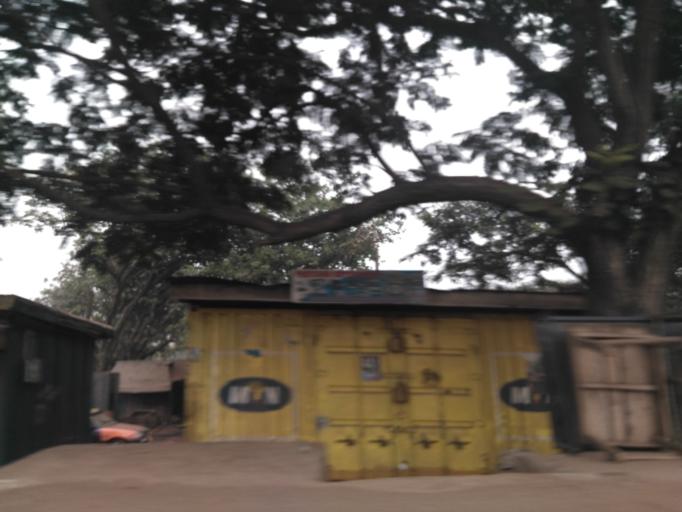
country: GH
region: Ashanti
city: Kumasi
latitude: 6.7101
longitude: -1.6316
